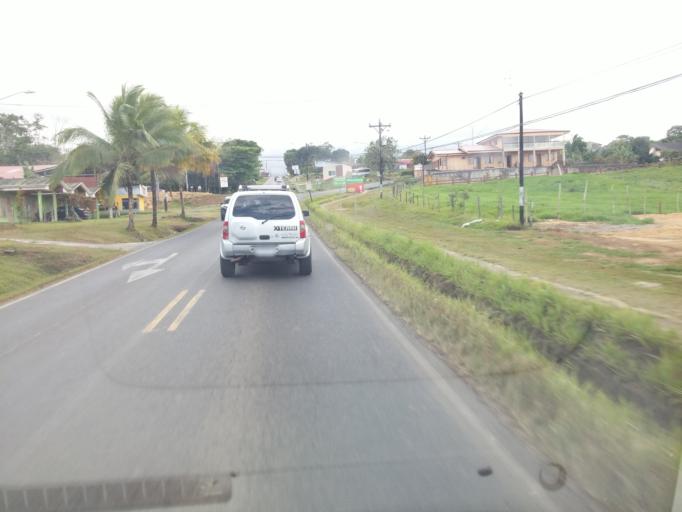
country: CR
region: Alajuela
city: Pital
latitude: 10.3812
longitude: -84.3396
